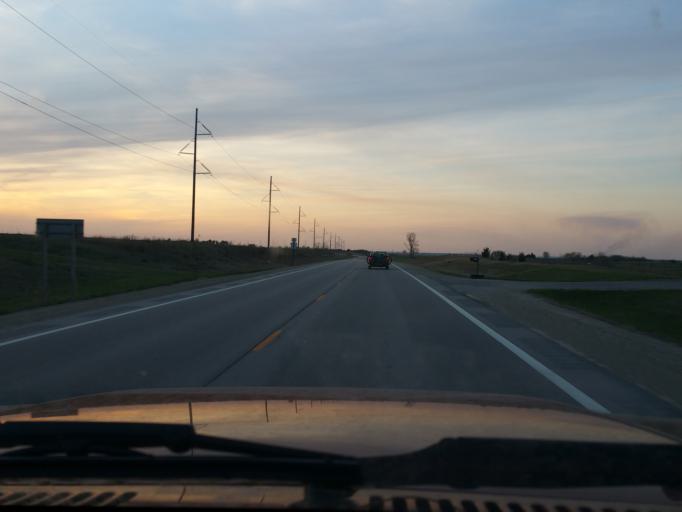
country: US
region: Kansas
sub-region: Riley County
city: Manhattan
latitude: 39.2647
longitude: -96.6832
